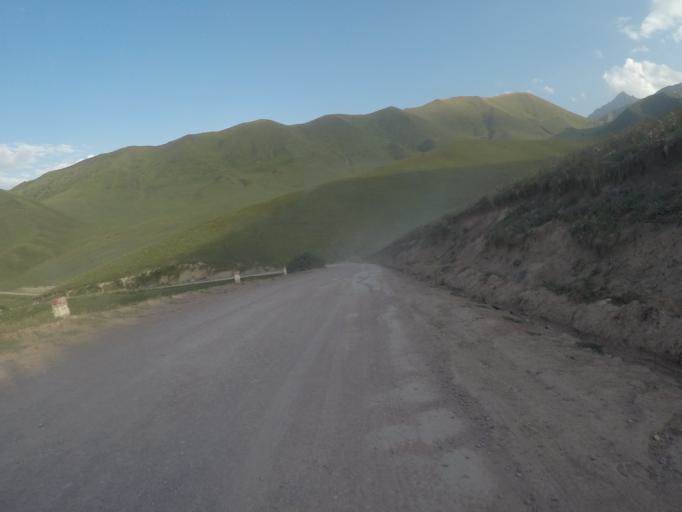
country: KG
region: Chuy
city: Bishkek
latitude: 42.6409
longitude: 74.6349
